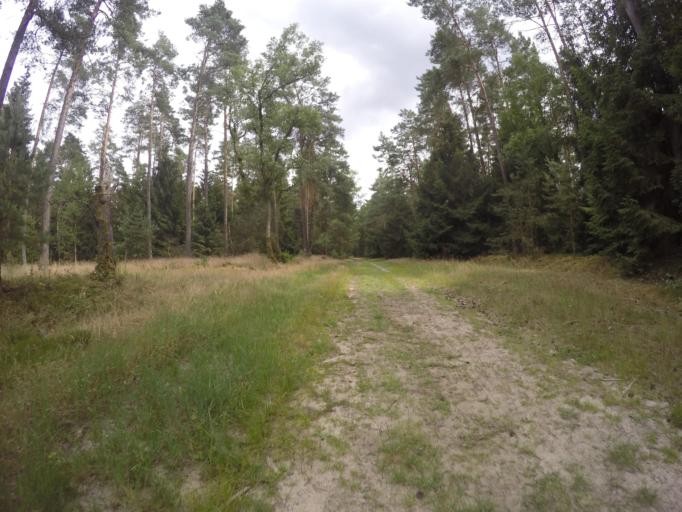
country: DE
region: Lower Saxony
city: Thomasburg
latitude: 53.2370
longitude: 10.6903
